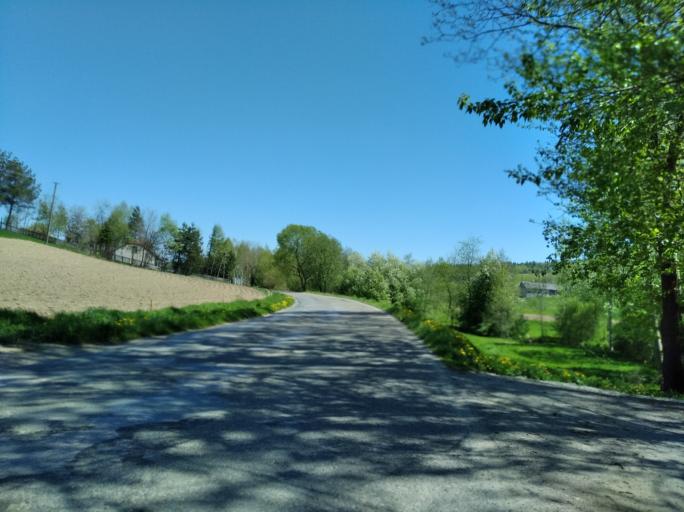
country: PL
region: Subcarpathian Voivodeship
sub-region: Powiat debicki
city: Brzostek
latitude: 49.9160
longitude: 21.4282
